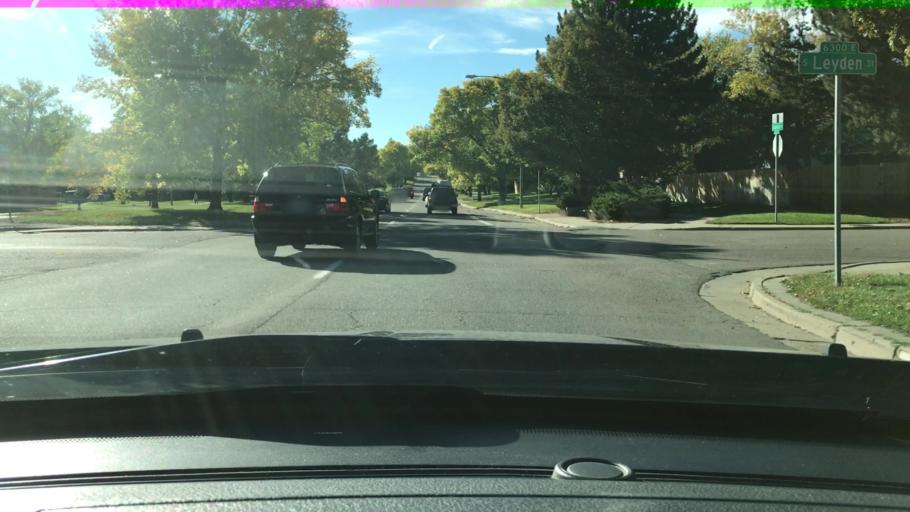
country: US
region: Colorado
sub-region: Arapahoe County
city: Glendale
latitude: 39.7114
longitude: -104.9152
